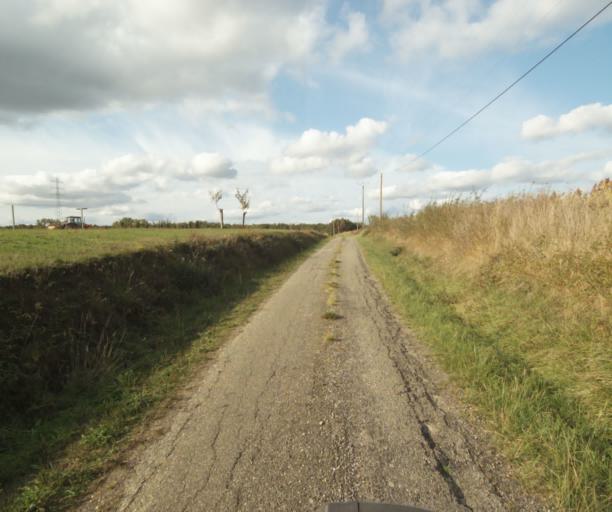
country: FR
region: Midi-Pyrenees
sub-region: Departement du Tarn-et-Garonne
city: Verdun-sur-Garonne
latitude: 43.8418
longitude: 1.1464
